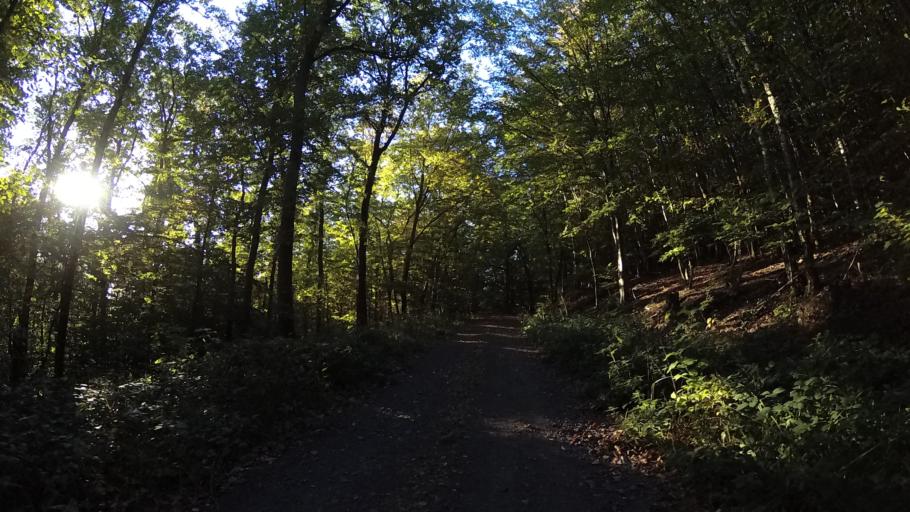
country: DE
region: Saarland
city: Ottweiler
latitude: 49.4309
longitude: 7.1831
